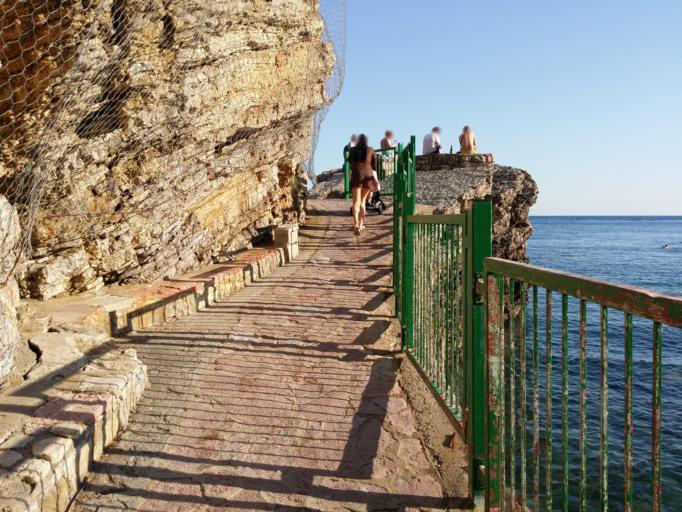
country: ME
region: Budva
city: Budva
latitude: 42.2769
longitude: 18.8334
